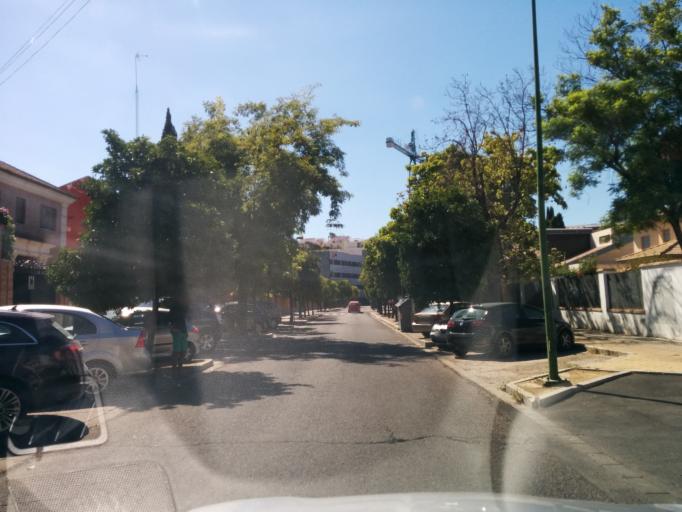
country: ES
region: Andalusia
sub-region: Provincia de Sevilla
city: Sevilla
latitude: 37.3599
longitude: -5.9830
